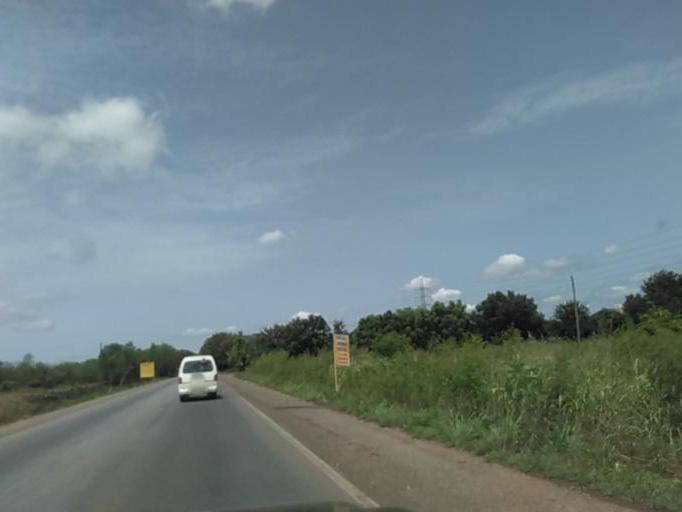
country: GH
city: Akropong
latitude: 6.1341
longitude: 0.0507
